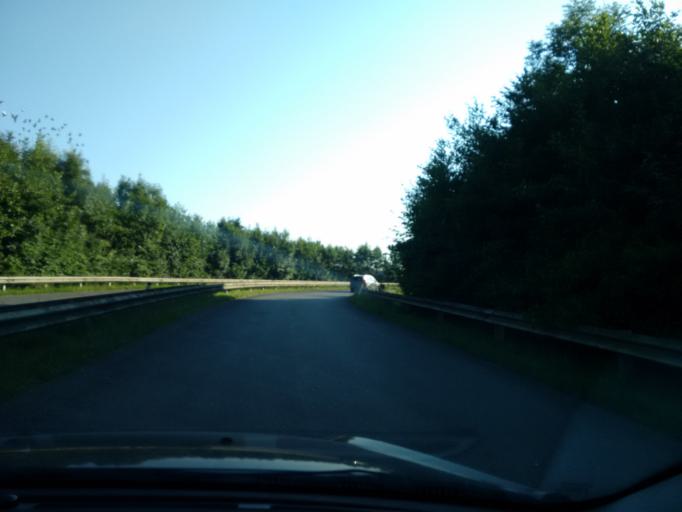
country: AT
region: Upper Austria
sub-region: Politischer Bezirk Grieskirchen
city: Bad Schallerbach
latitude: 48.1952
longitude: 13.9260
